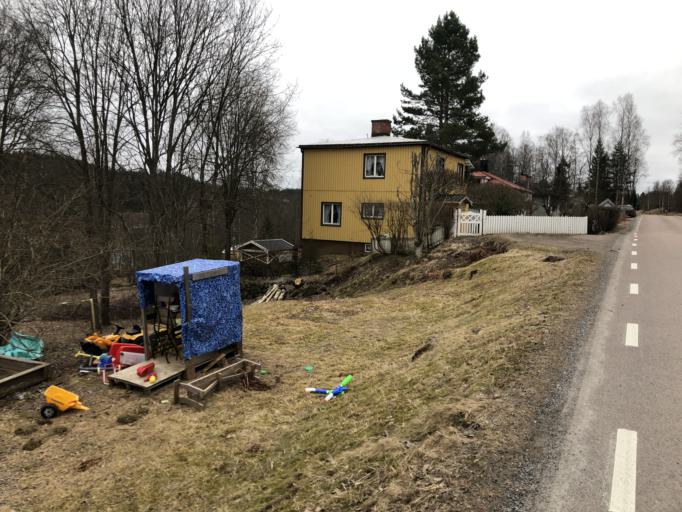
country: SE
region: Vaermland
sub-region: Filipstads Kommun
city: Lesjofors
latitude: 59.9742
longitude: 14.1845
